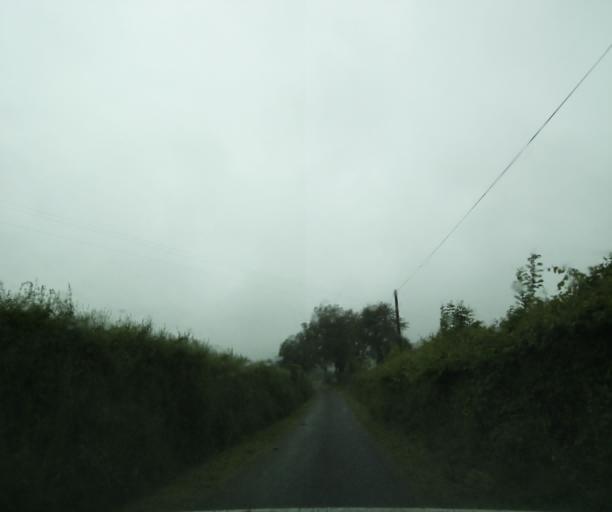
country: FR
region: Bourgogne
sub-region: Departement de Saone-et-Loire
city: Charolles
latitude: 46.4054
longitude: 4.3920
